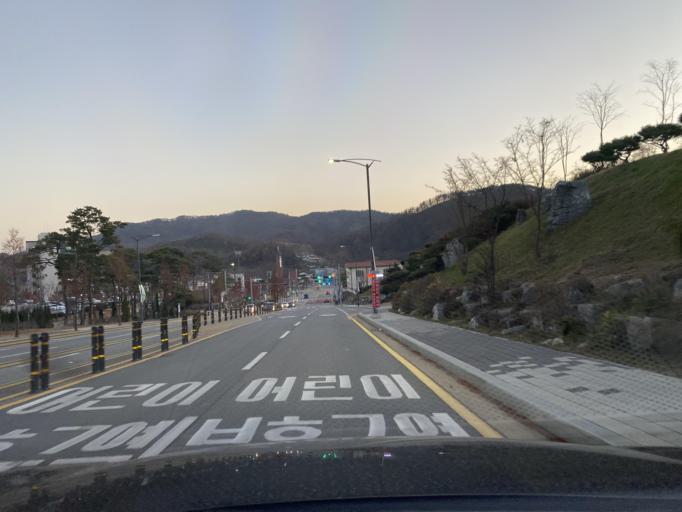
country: KR
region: Chungcheongnam-do
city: Yesan
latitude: 36.6814
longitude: 126.8434
